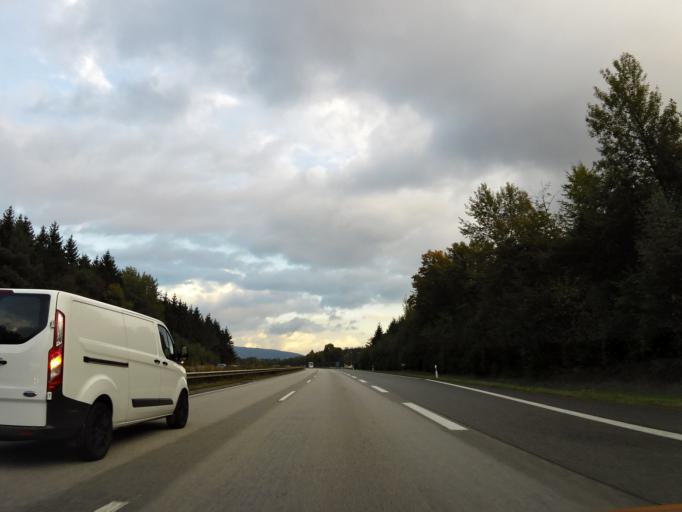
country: DE
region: Rheinland-Pfalz
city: Liebshausen
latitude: 50.0394
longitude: 7.6420
